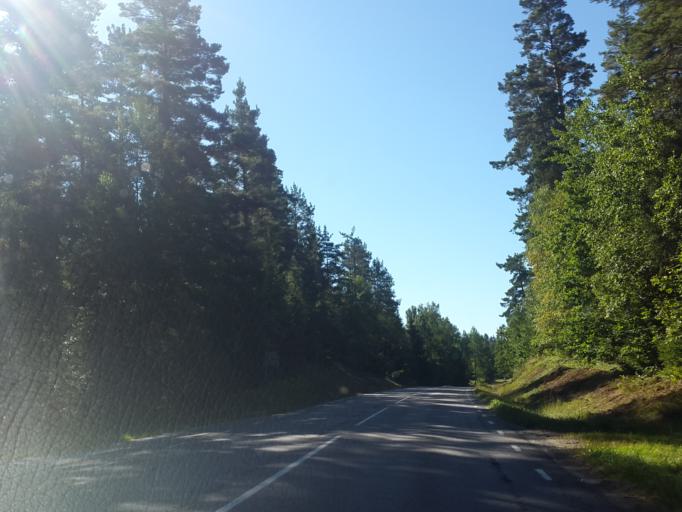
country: SE
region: Vaestra Goetaland
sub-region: Herrljunga Kommun
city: Herrljunga
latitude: 58.0712
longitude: 13.0417
